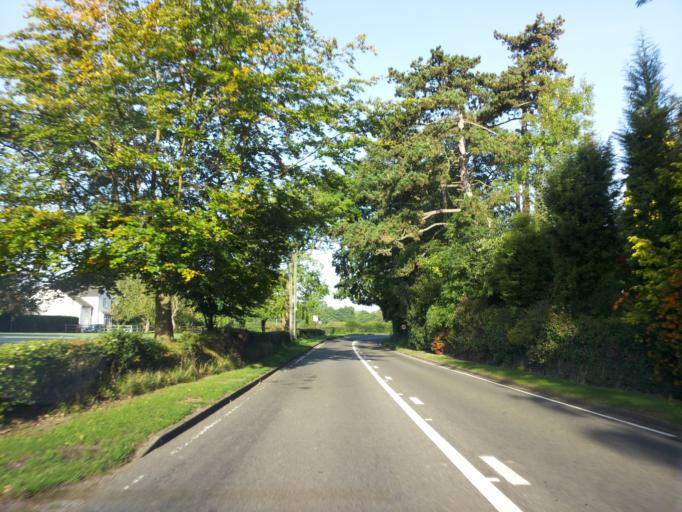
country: GB
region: England
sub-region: Solihull
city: Knowle
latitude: 52.3652
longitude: -1.7090
